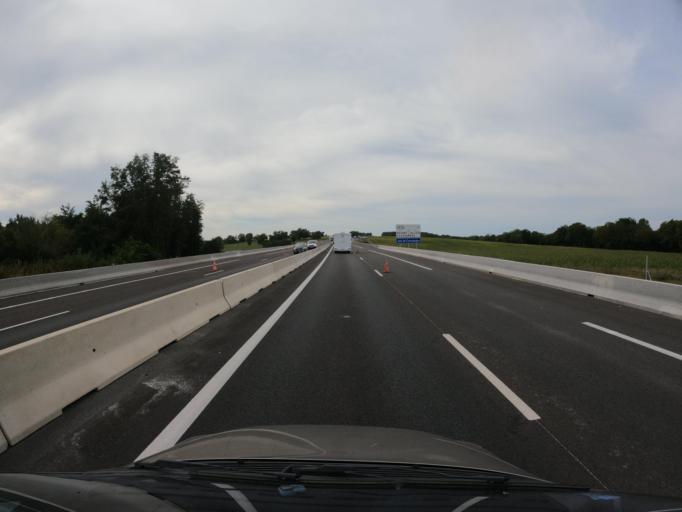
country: FR
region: Auvergne
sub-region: Departement de l'Allier
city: Bessay-sur-Allier
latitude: 46.4734
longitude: 3.3046
